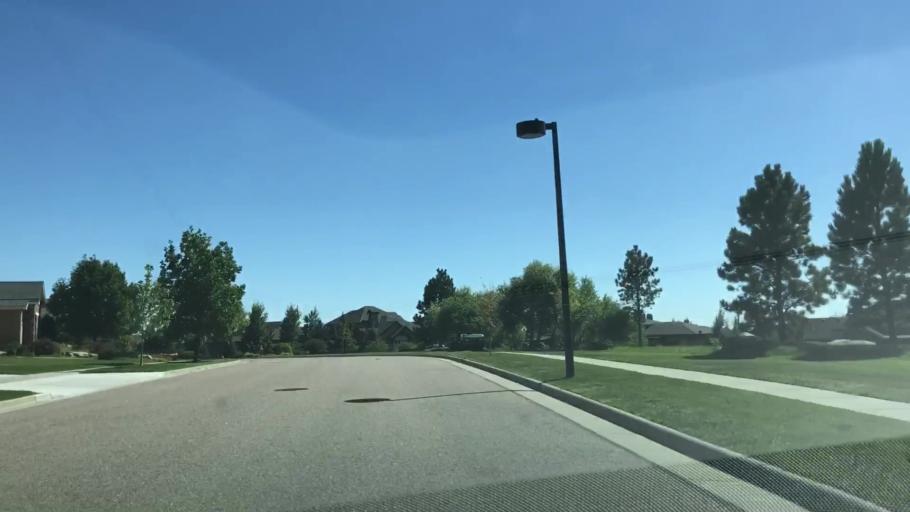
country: US
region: Colorado
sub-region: Weld County
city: Windsor
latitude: 40.5317
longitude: -104.9571
